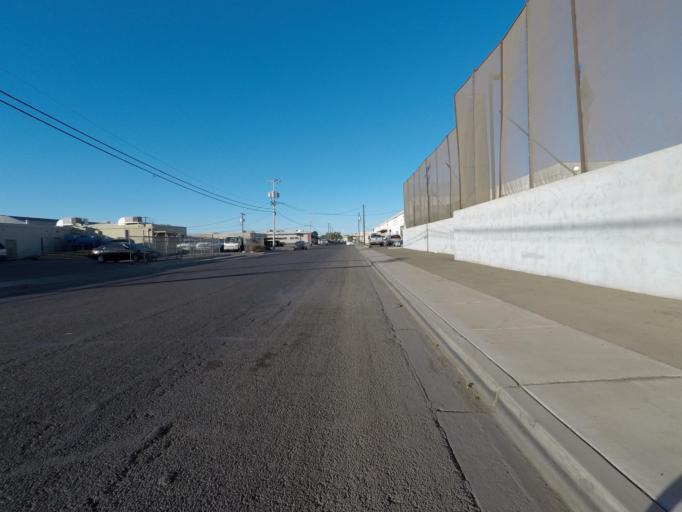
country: US
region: Arizona
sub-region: Maricopa County
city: Phoenix
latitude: 33.4685
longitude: -112.1063
